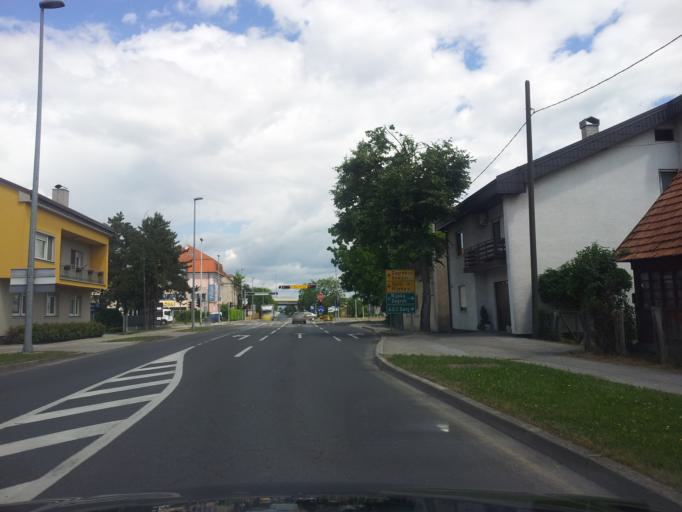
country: HR
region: Karlovacka
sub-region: Grad Karlovac
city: Karlovac
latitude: 45.5106
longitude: 15.5475
